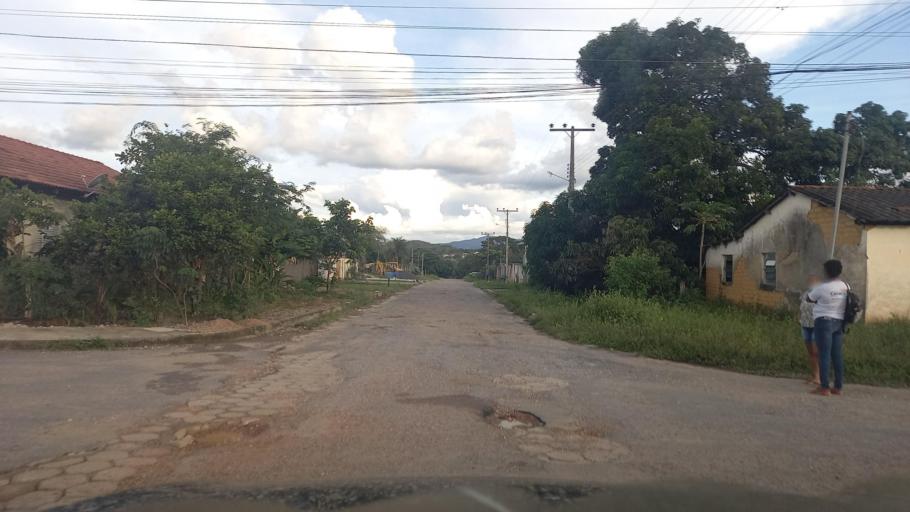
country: BR
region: Goias
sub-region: Cavalcante
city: Cavalcante
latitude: -13.7921
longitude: -47.4572
